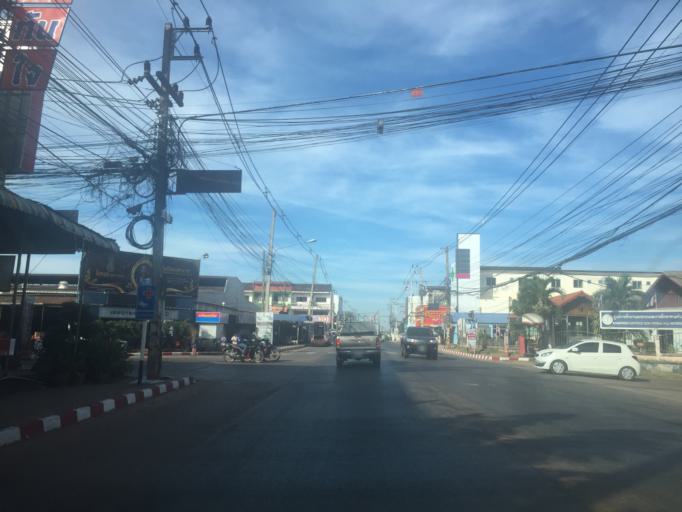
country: TH
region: Changwat Udon Thani
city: Kumphawapi
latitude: 17.1109
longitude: 103.0156
